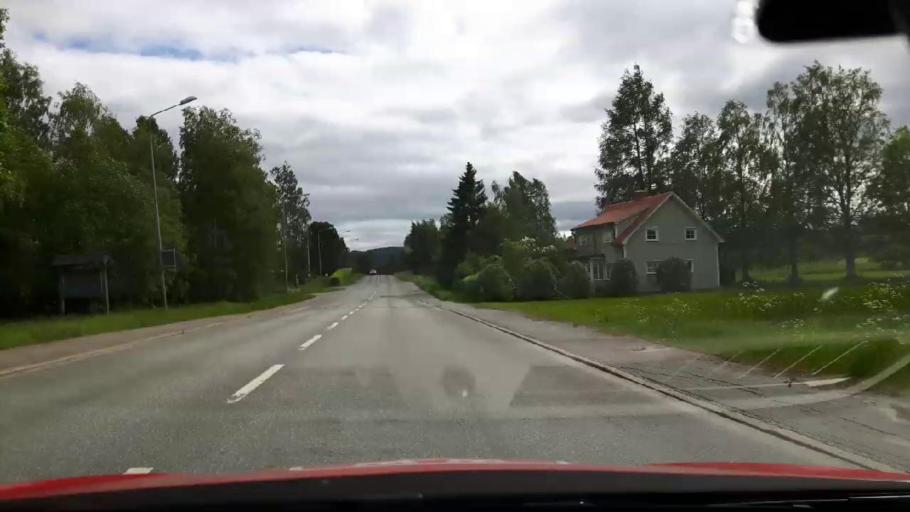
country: SE
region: Jaemtland
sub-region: Ragunda Kommun
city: Hammarstrand
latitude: 63.1009
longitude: 16.3577
